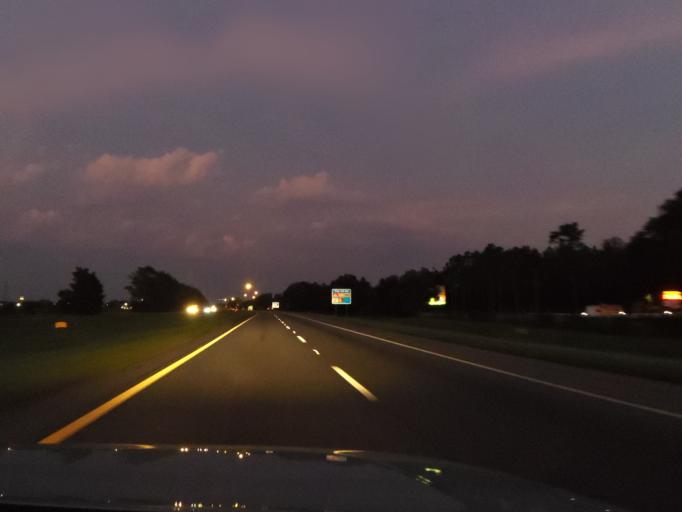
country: US
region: Florida
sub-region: Madison County
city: Madison
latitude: 30.3974
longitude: -83.3686
